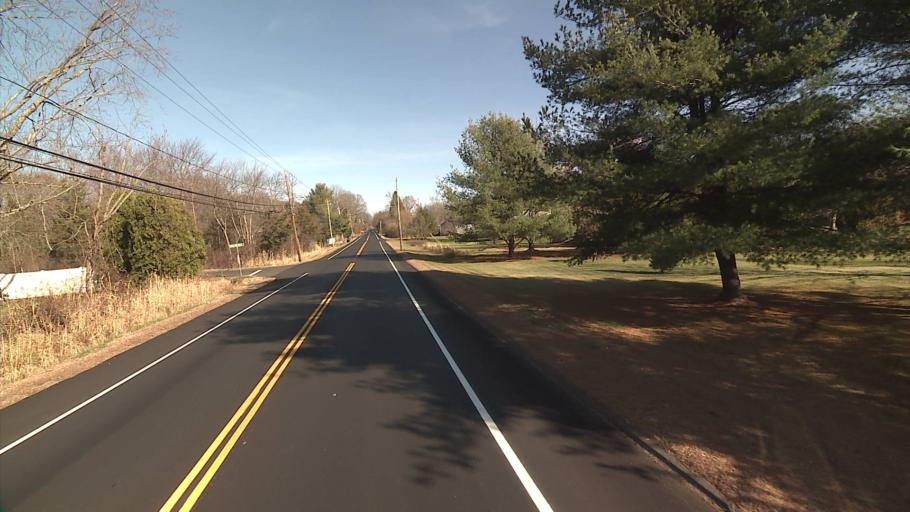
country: US
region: Connecticut
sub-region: New Haven County
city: Wallingford Center
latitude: 41.4169
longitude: -72.7458
